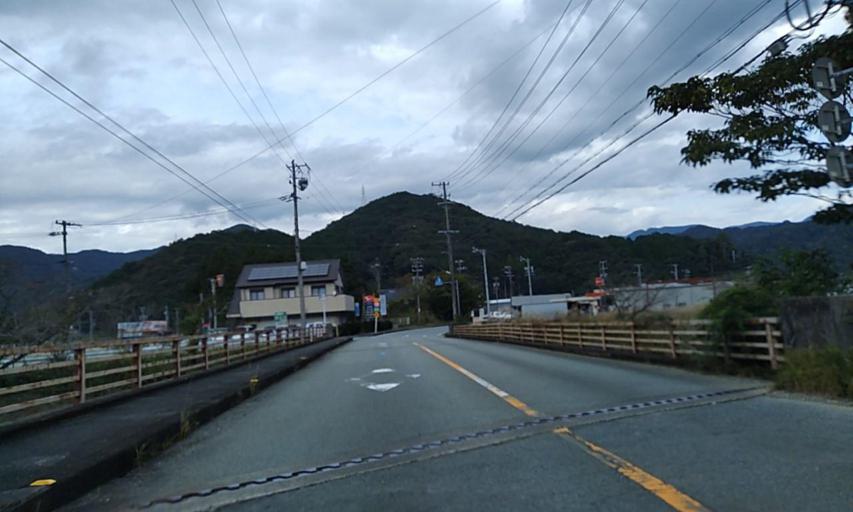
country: JP
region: Mie
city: Ise
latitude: 34.2761
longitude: 136.4923
